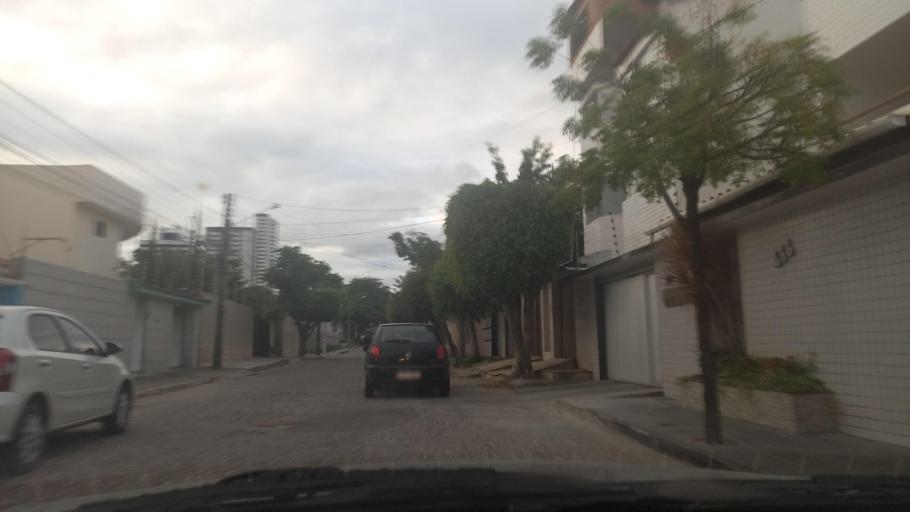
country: BR
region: Pernambuco
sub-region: Caruaru
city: Caruaru
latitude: -8.2705
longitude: -35.9654
